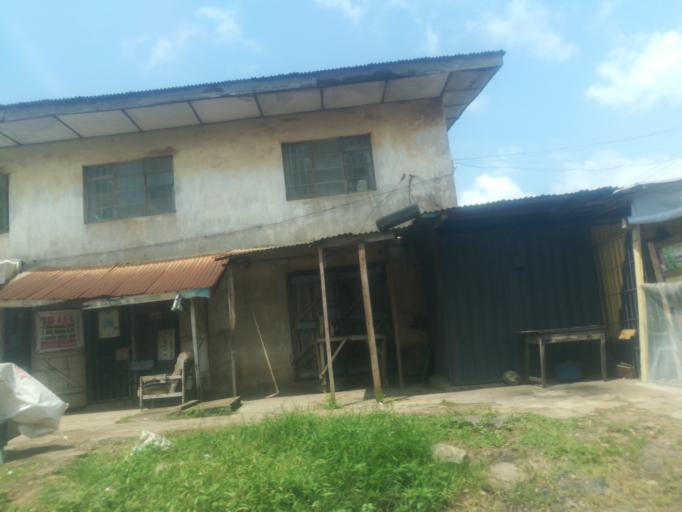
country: NG
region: Oyo
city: Ibadan
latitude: 7.3658
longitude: 3.8782
